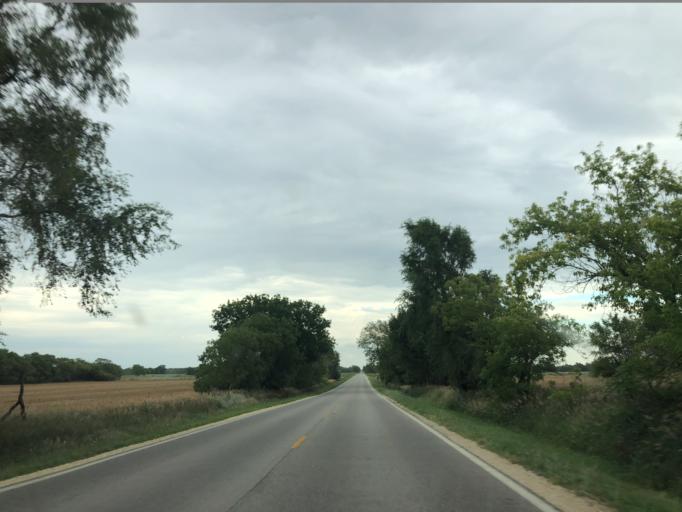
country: US
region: Kansas
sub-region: Reno County
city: Nickerson
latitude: 38.1449
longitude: -98.1380
